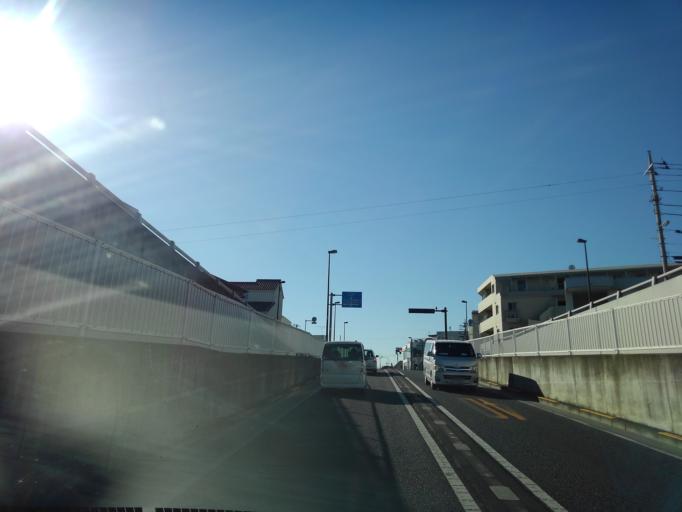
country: JP
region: Tokyo
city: Hino
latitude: 35.7079
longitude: 139.3782
